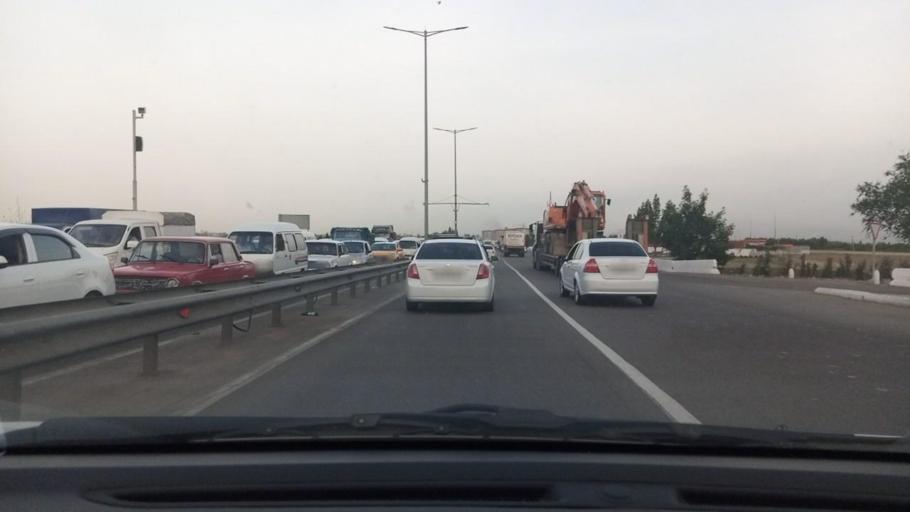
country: UZ
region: Toshkent
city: Ohangaron
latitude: 40.9202
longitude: 69.5976
